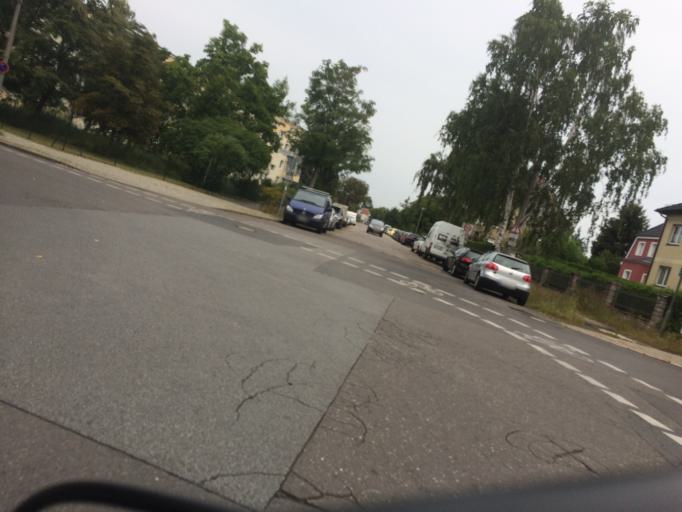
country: DE
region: Berlin
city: Wilhelmsruh
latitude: 52.5867
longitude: 13.3743
